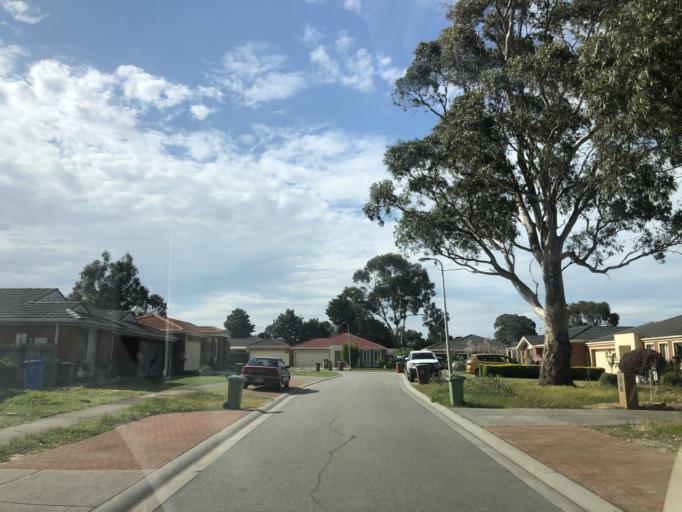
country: AU
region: Victoria
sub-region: Casey
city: Hampton Park
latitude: -38.0375
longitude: 145.2521
